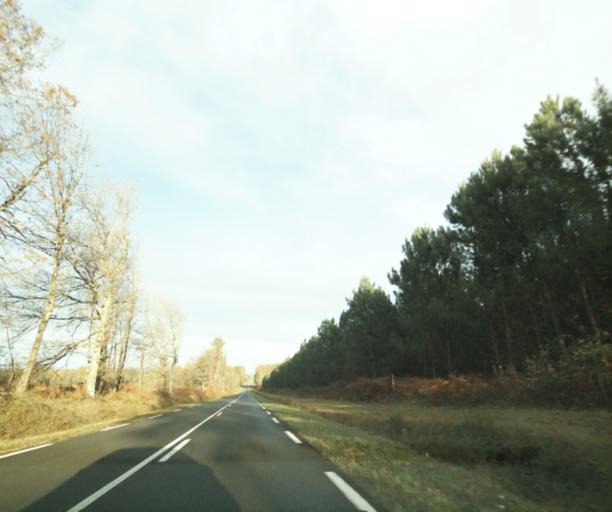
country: FR
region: Aquitaine
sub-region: Departement des Landes
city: Gabarret
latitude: 43.9579
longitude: -0.0187
